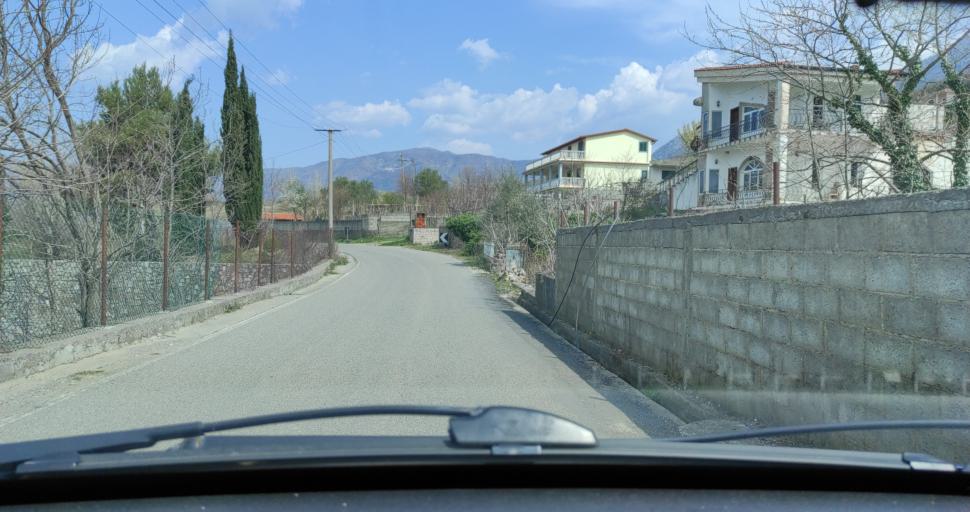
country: AL
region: Lezhe
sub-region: Rrethi i Lezhes
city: Kallmeti i Madh
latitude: 41.8439
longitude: 19.6811
